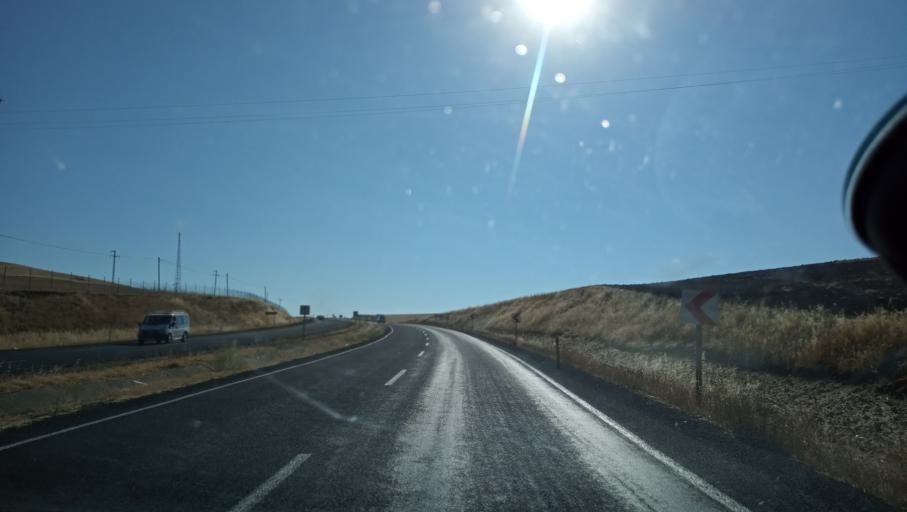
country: TR
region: Diyarbakir
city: Sur
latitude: 37.9916
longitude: 40.3937
